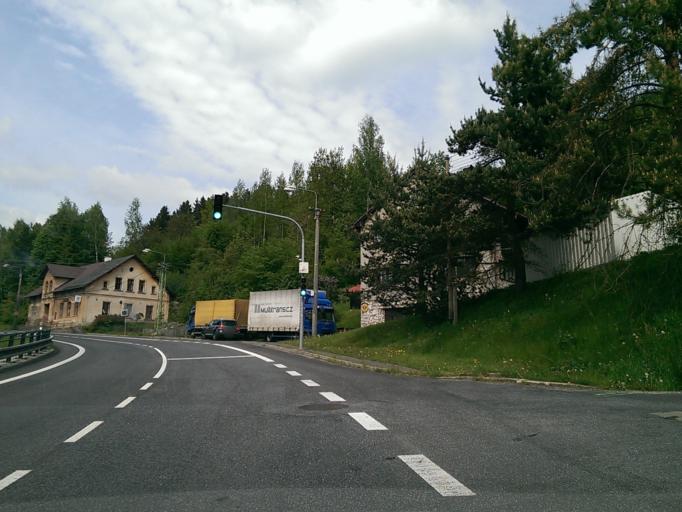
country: CZ
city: Pencin
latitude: 50.6793
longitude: 15.2671
